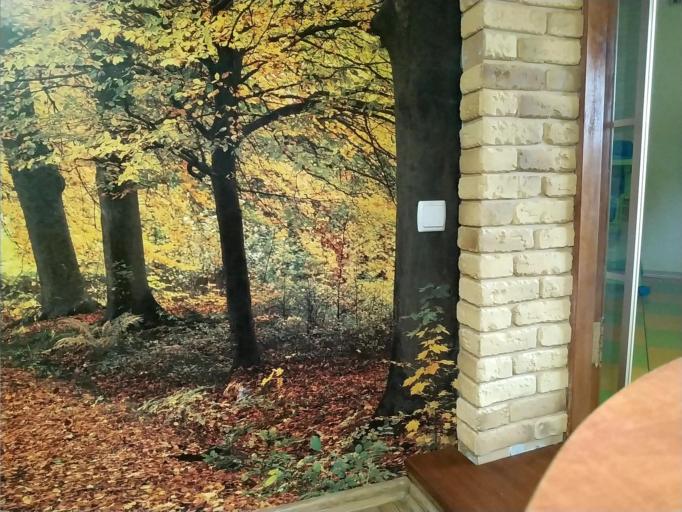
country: RU
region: Smolensk
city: Dorogobuzh
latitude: 54.9475
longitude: 33.2969
